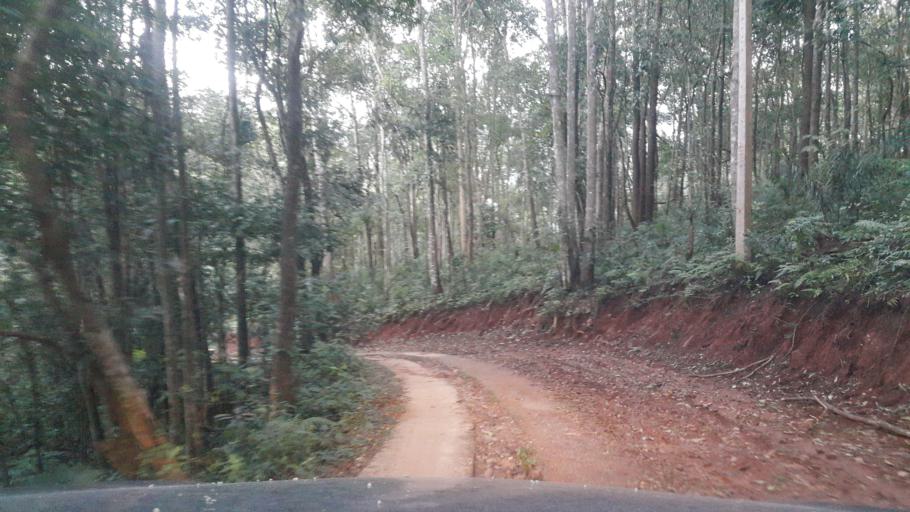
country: TH
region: Chiang Mai
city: Samoeng
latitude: 19.0083
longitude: 98.6664
